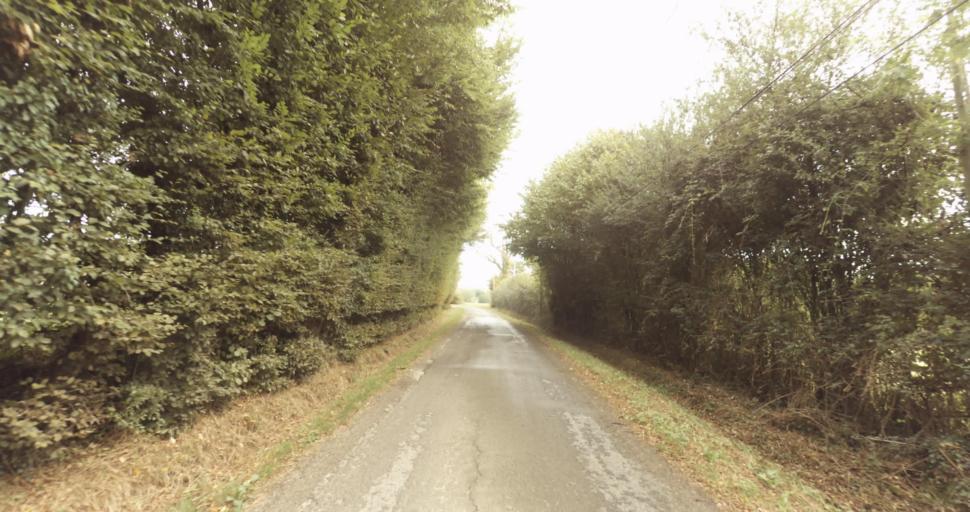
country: FR
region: Lower Normandy
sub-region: Departement de l'Orne
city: Sainte-Gauburge-Sainte-Colombe
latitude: 48.7232
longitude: 0.4781
